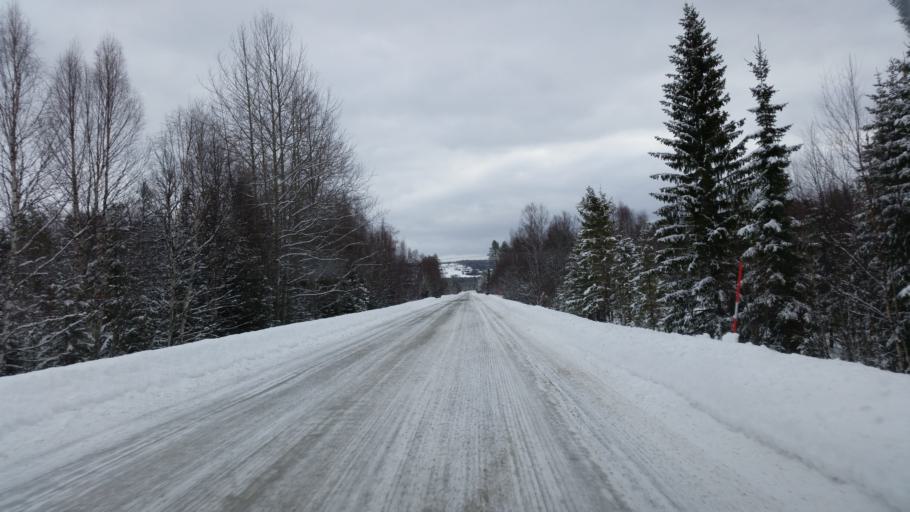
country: SE
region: Jaemtland
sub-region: Bergs Kommun
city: Hoverberg
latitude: 62.4745
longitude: 14.3838
